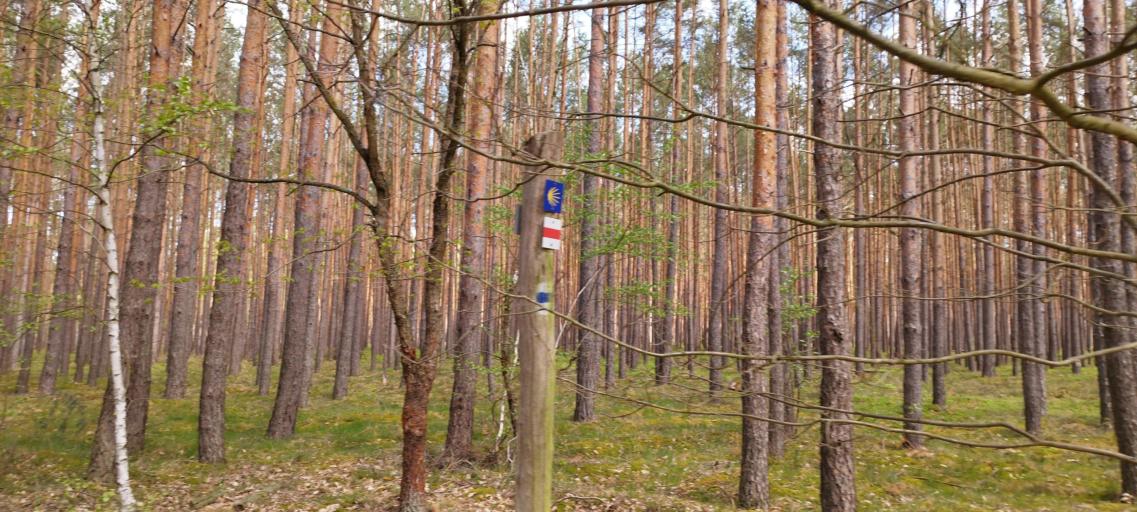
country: DE
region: Brandenburg
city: Grunheide
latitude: 52.3900
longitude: 13.8417
